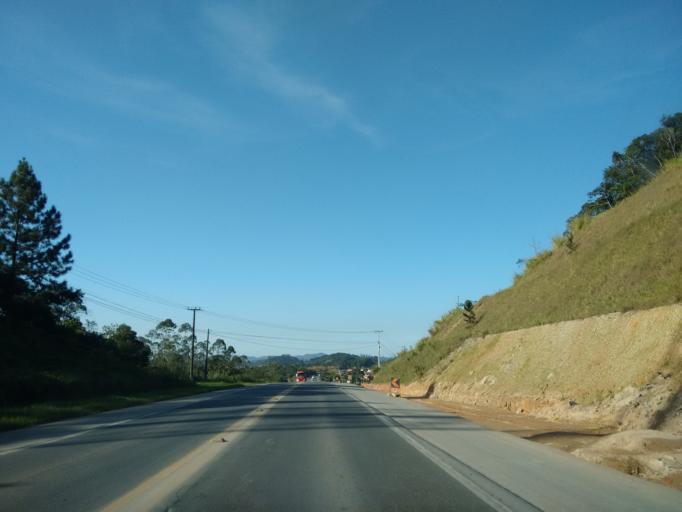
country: BR
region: Santa Catarina
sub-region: Guaramirim
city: Guaramirim
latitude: -26.4574
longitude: -48.9339
